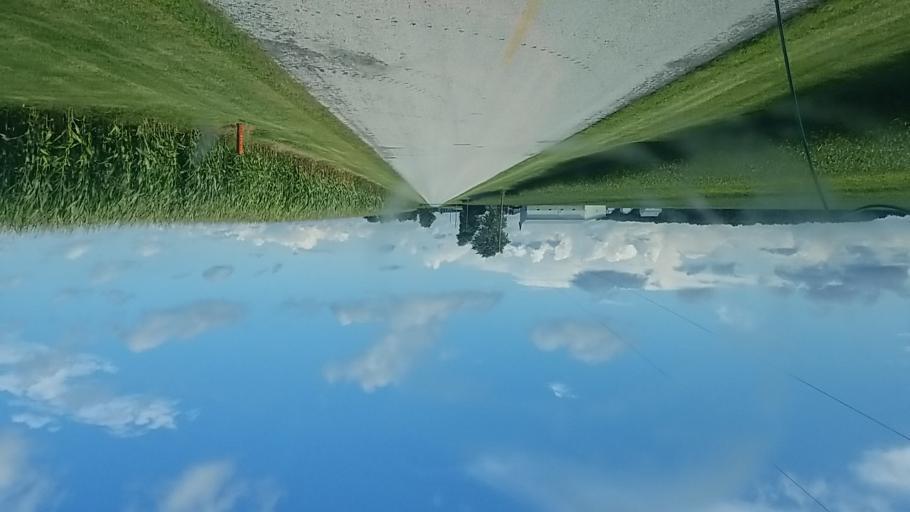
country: US
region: Ohio
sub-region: Hardin County
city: Forest
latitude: 40.7374
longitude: -83.5159
